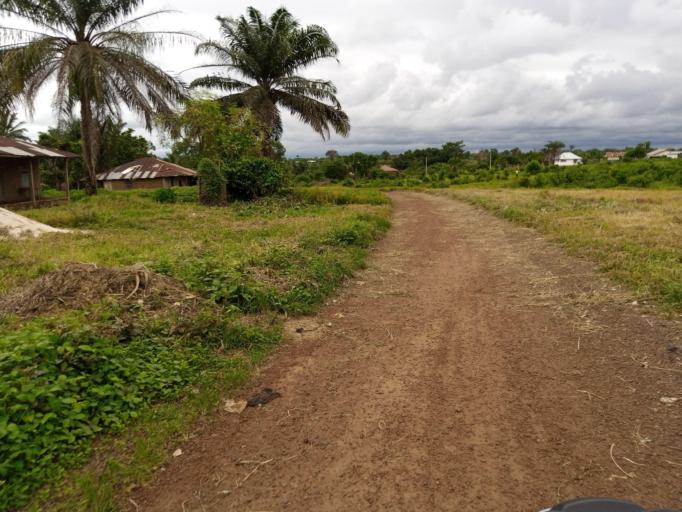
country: SL
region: Southern Province
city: Moyamba
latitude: 8.1667
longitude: -12.4260
